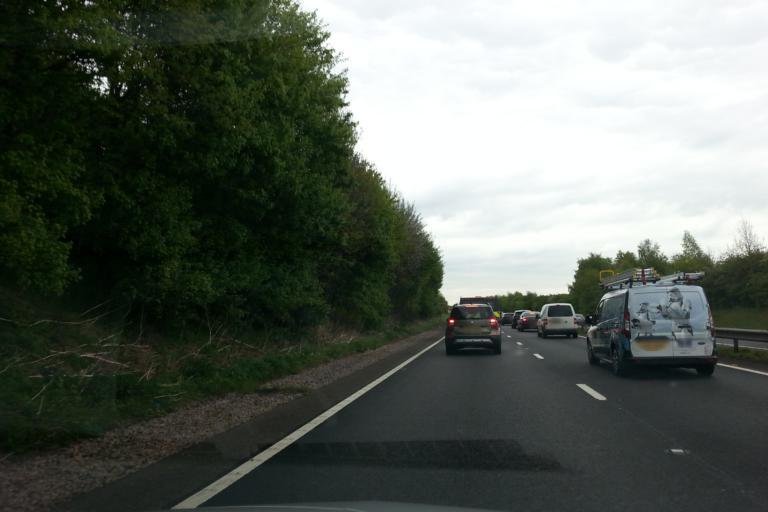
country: GB
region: England
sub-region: Leicestershire
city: Castle Donington
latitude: 52.8024
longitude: -1.3301
